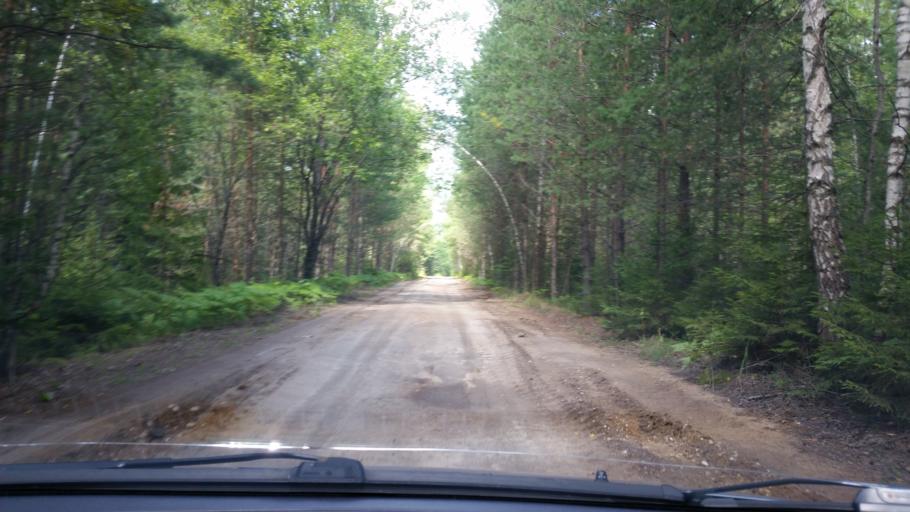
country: RU
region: Moskovskaya
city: Pushchino
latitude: 54.9219
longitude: 37.6855
